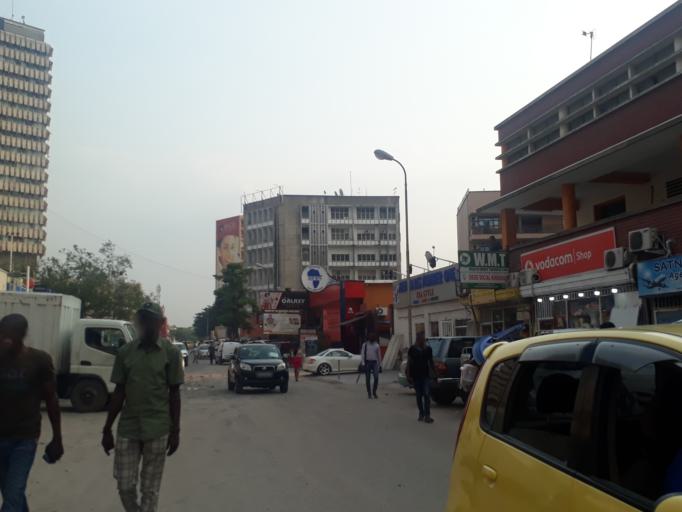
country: CD
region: Kinshasa
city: Kinshasa
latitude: -4.3020
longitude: 15.3105
